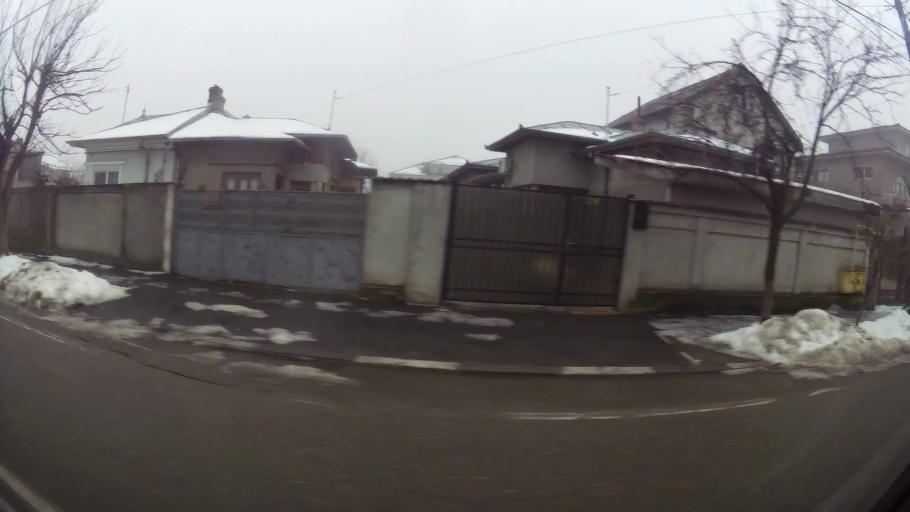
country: RO
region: Ilfov
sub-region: Comuna Chiajna
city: Chiajna
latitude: 44.4601
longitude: 25.9788
